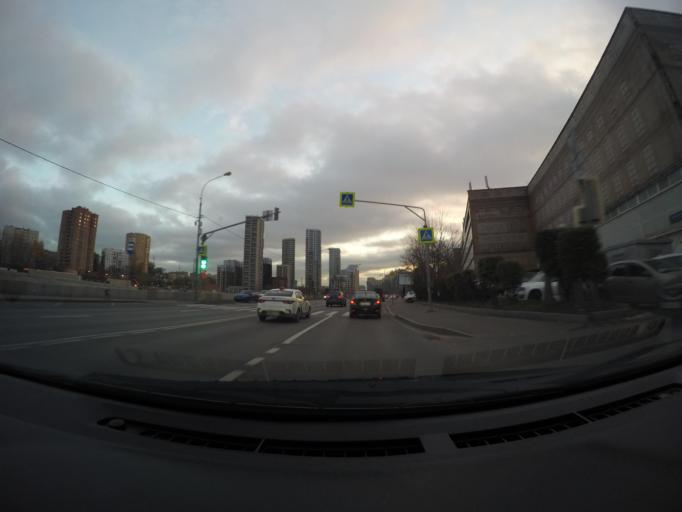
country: RU
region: Moscow
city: Taganskiy
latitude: 55.7230
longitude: 37.6561
